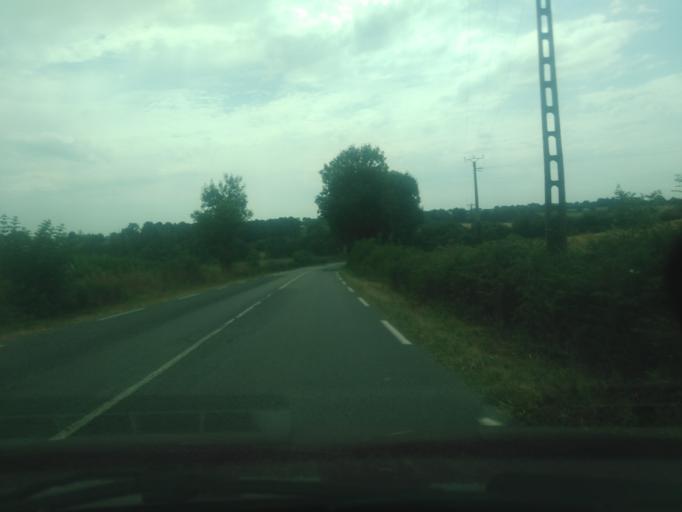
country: FR
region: Pays de la Loire
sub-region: Departement de la Vendee
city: La Tardiere
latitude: 46.6506
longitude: -0.7043
